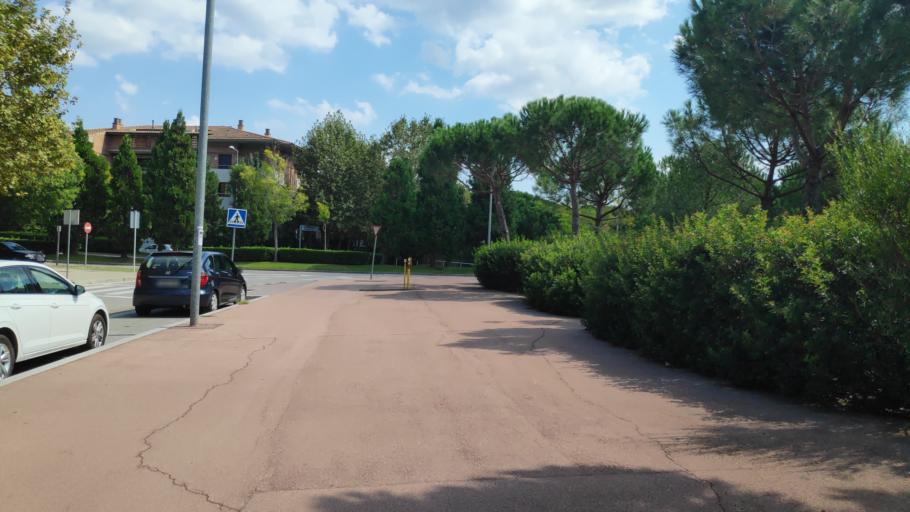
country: ES
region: Catalonia
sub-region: Provincia de Barcelona
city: Sant Cugat del Valles
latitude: 41.4756
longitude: 2.0681
